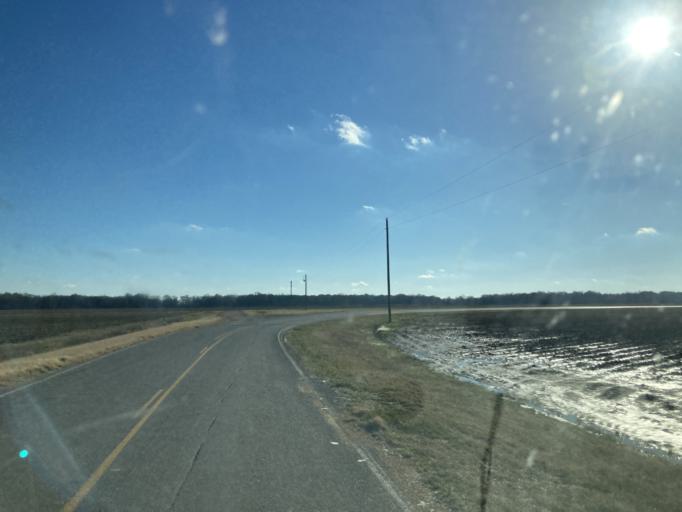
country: US
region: Mississippi
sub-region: Yazoo County
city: Yazoo City
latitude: 32.9250
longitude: -90.5058
